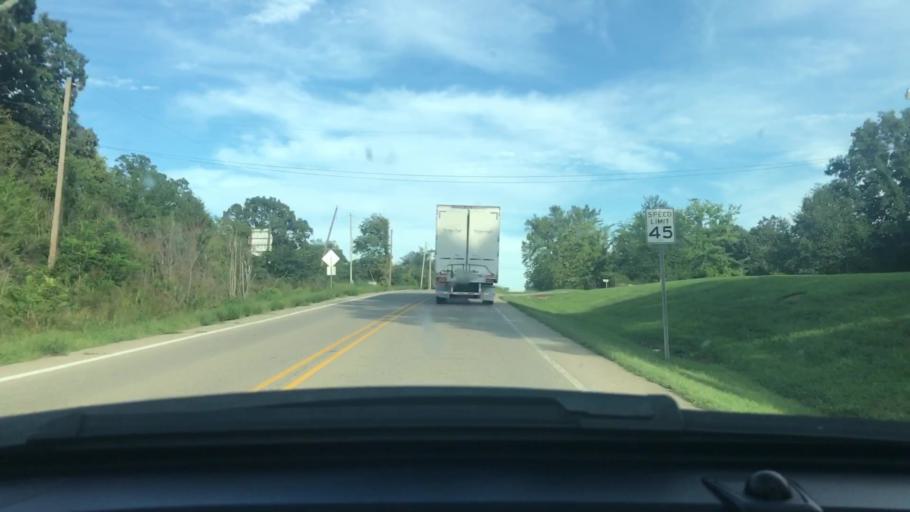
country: US
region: Arkansas
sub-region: Sharp County
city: Cherokee Village
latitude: 36.2396
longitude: -91.2624
